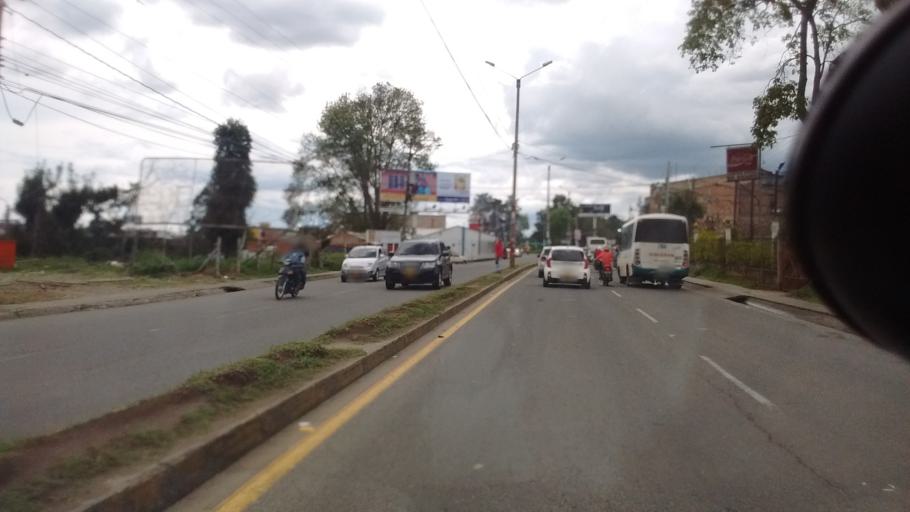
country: CO
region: Cauca
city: Popayan
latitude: 2.4813
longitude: -76.5723
